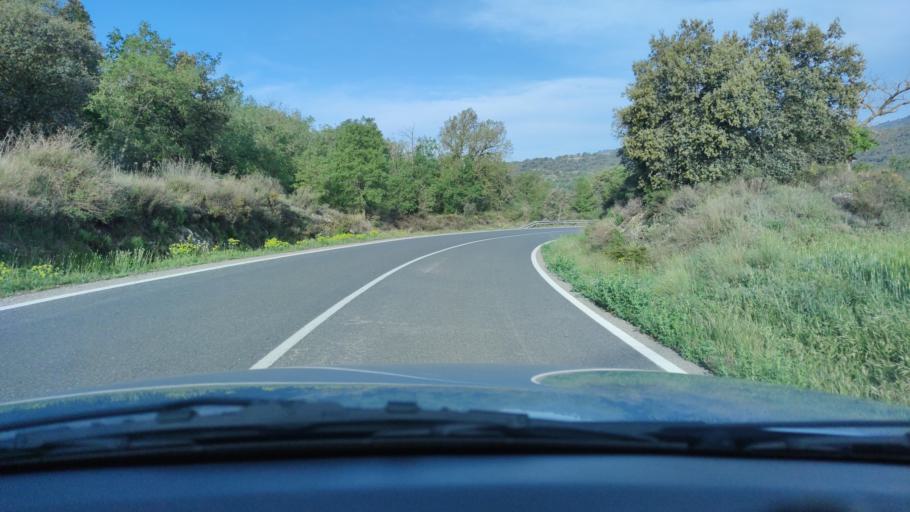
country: ES
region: Catalonia
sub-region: Provincia de Lleida
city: Ponts
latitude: 41.8943
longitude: 1.1729
